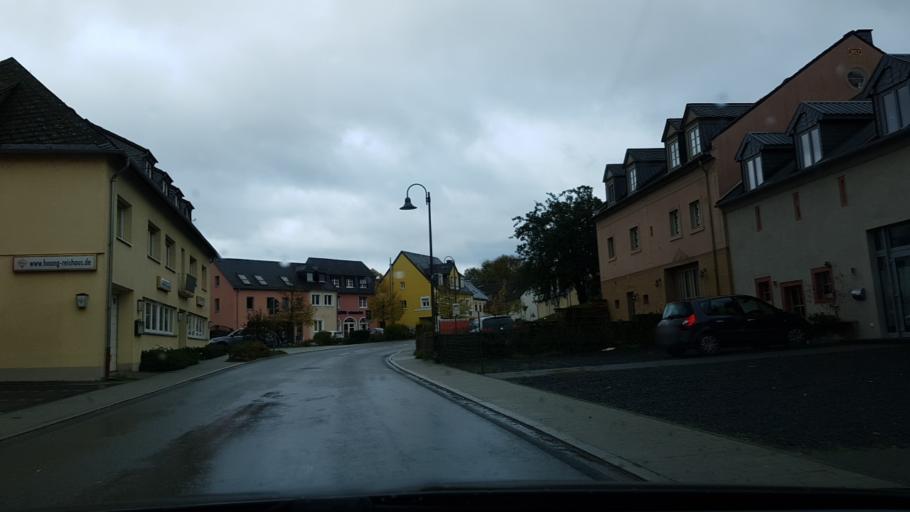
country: DE
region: Rheinland-Pfalz
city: Hetzerath
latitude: 49.8755
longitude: 6.8159
